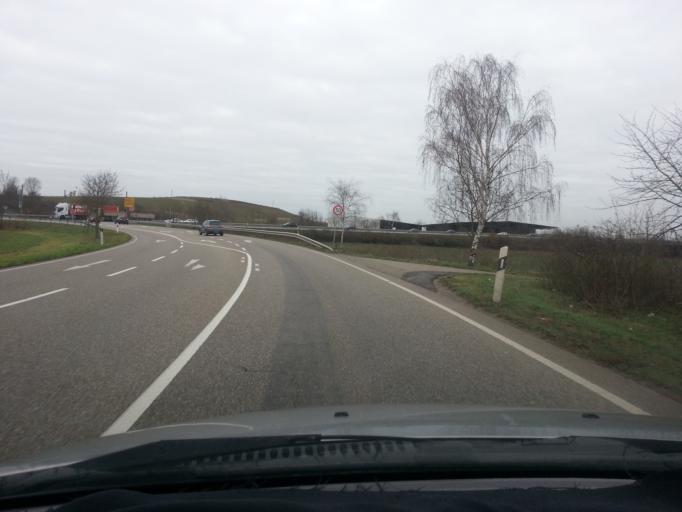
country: DE
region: Baden-Wuerttemberg
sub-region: Karlsruhe Region
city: Neulussheim
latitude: 49.3058
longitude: 8.5305
